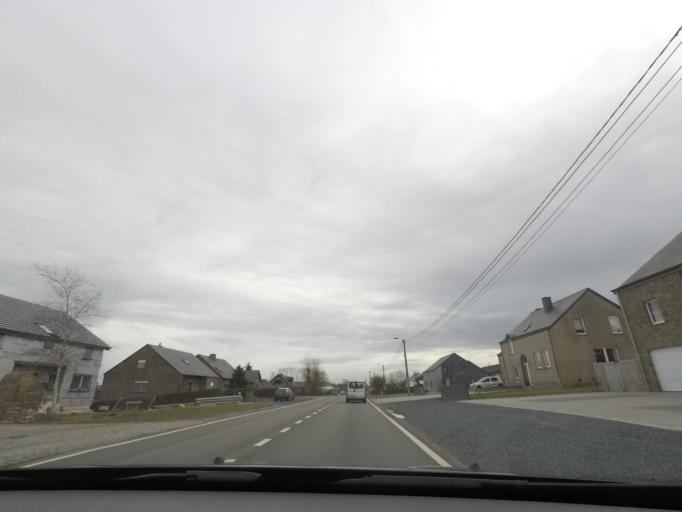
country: BE
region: Wallonia
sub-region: Province du Luxembourg
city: Bastogne
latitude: 49.9914
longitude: 5.7447
